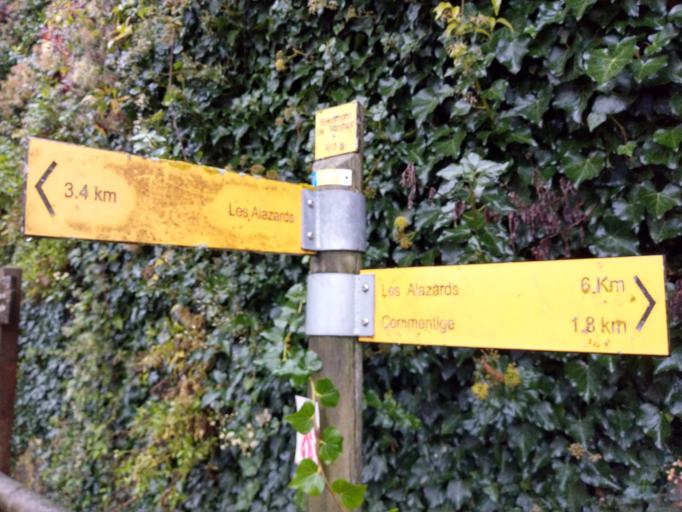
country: FR
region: Provence-Alpes-Cote d'Azur
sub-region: Departement du Vaucluse
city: Malaucene
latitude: 44.1841
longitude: 5.1667
